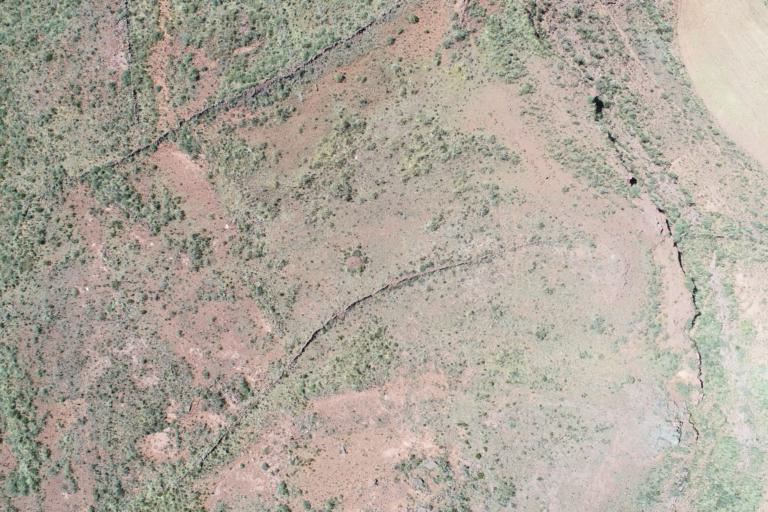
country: BO
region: La Paz
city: Tiahuanaco
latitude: -16.6055
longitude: -68.7711
